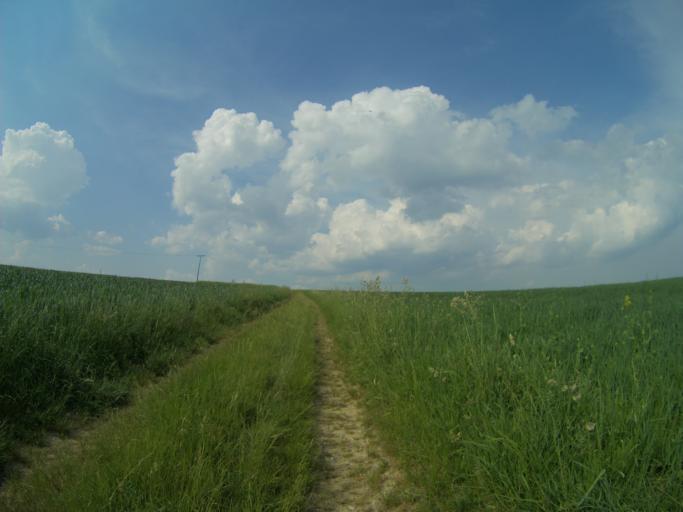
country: DE
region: Bavaria
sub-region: Upper Bavaria
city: Marzling
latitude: 48.4299
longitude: 11.7997
